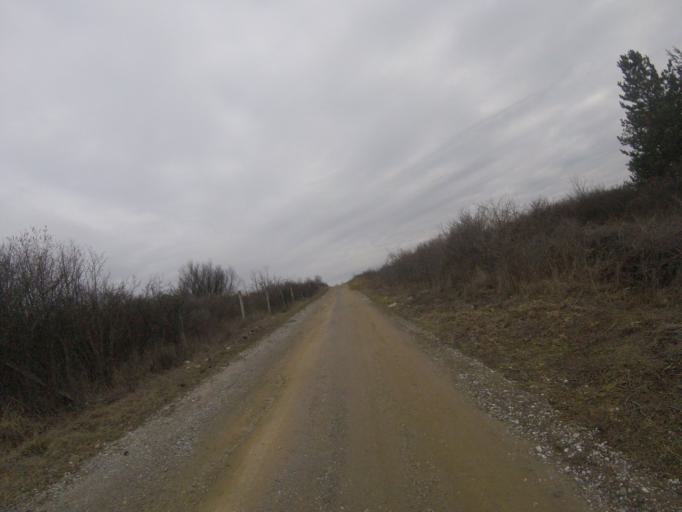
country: HU
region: Heves
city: Egerszalok
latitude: 47.8623
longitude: 20.3368
